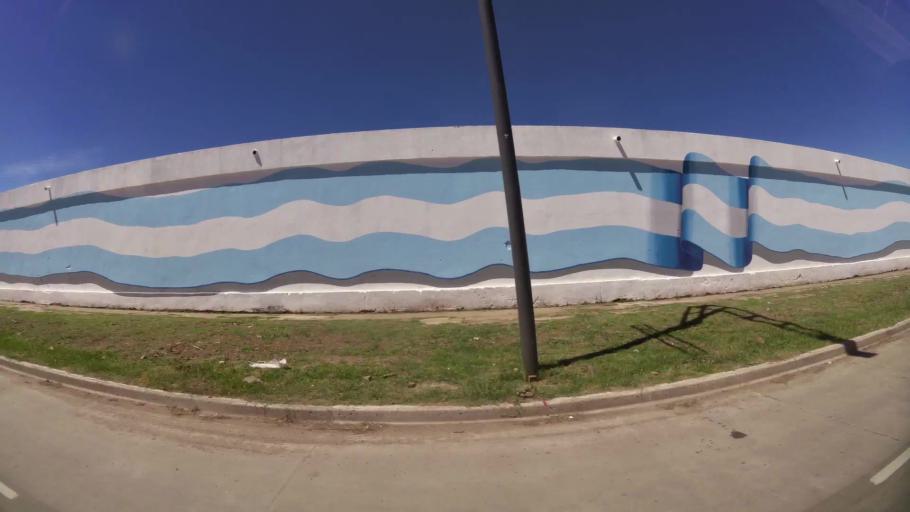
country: AR
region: Santa Fe
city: Perez
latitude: -32.9596
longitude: -60.7147
